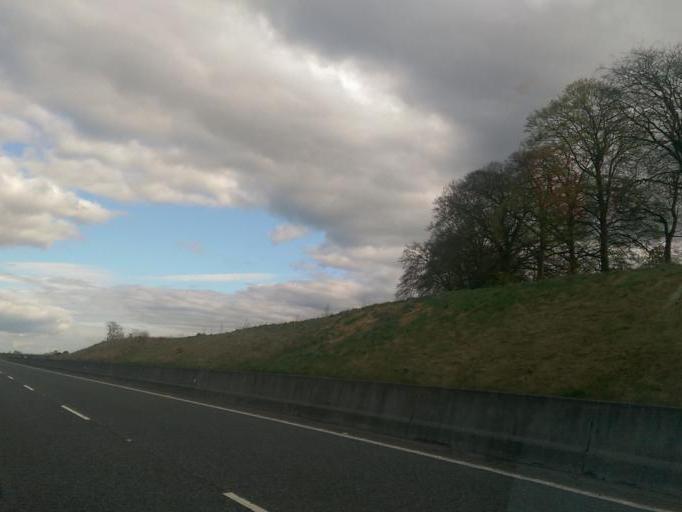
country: IE
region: Leinster
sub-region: Uibh Fhaili
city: Clara
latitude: 53.3835
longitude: -7.5789
